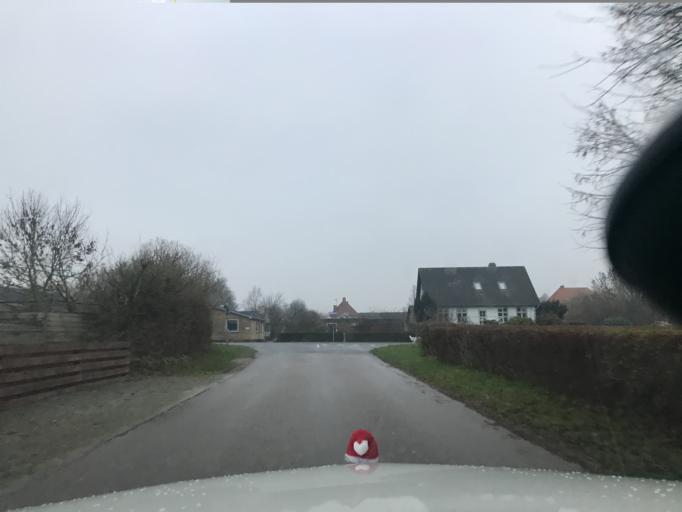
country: DK
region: South Denmark
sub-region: Sonderborg Kommune
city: Grasten
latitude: 54.8907
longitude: 9.5557
